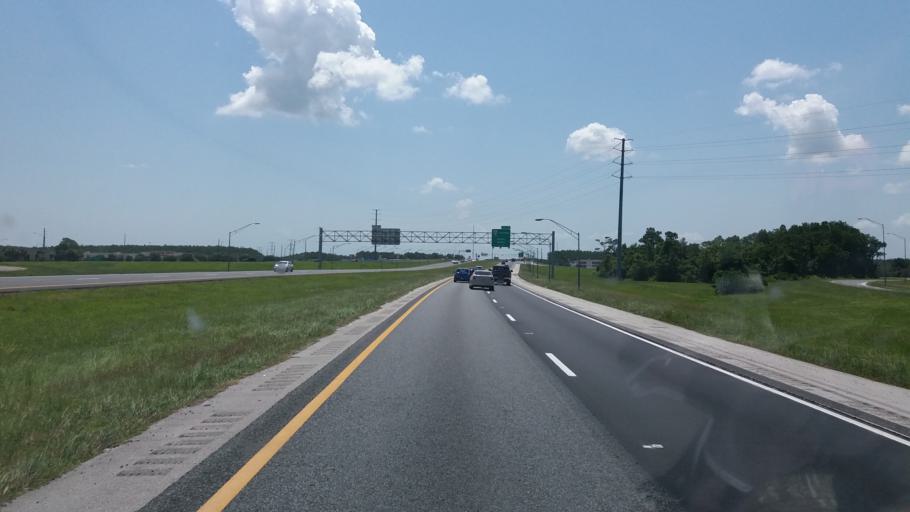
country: US
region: Florida
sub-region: Orange County
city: Hunters Creek
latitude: 28.3748
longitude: -81.4105
